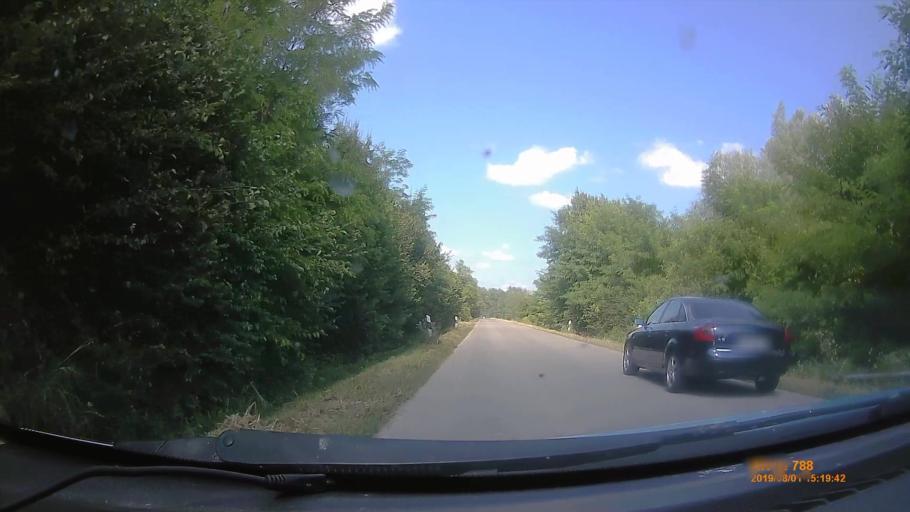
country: HU
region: Baranya
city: Sellye
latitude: 45.8567
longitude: 17.8264
